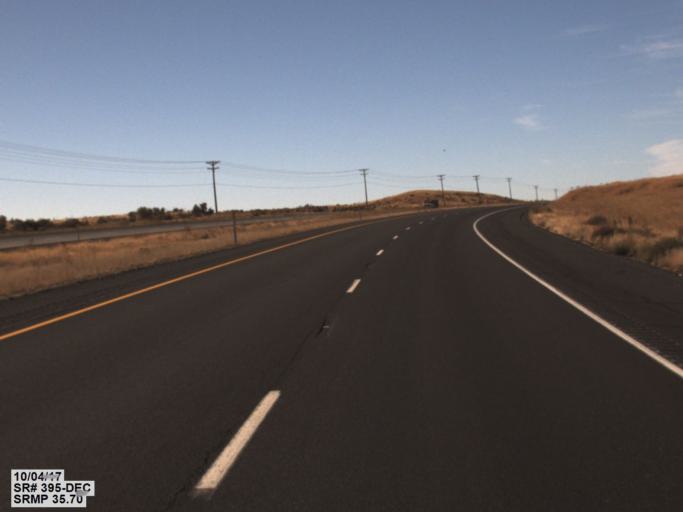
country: US
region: Washington
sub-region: Franklin County
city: Pasco
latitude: 46.4253
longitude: -119.0287
